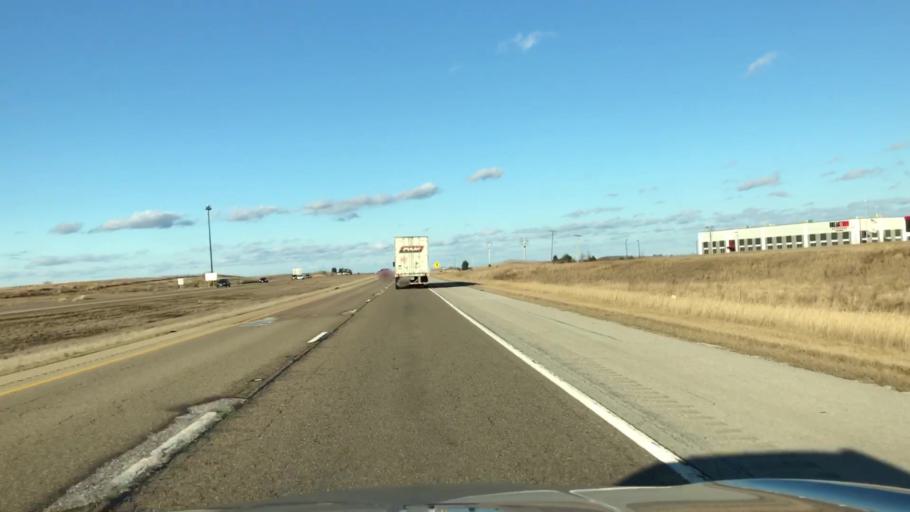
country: US
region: Illinois
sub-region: McLean County
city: Lexington
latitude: 40.6460
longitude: -88.8086
